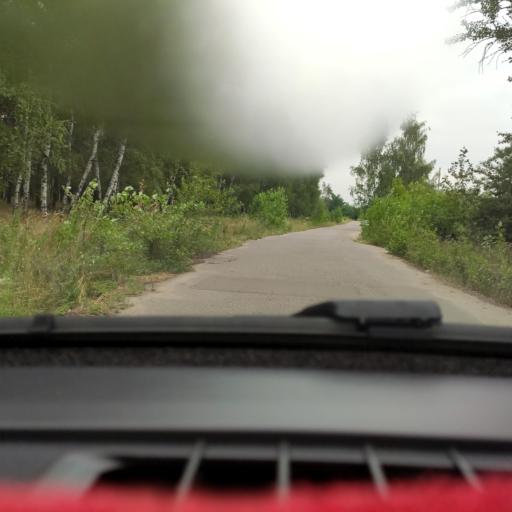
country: RU
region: Voronezj
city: Somovo
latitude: 51.7329
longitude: 39.3197
